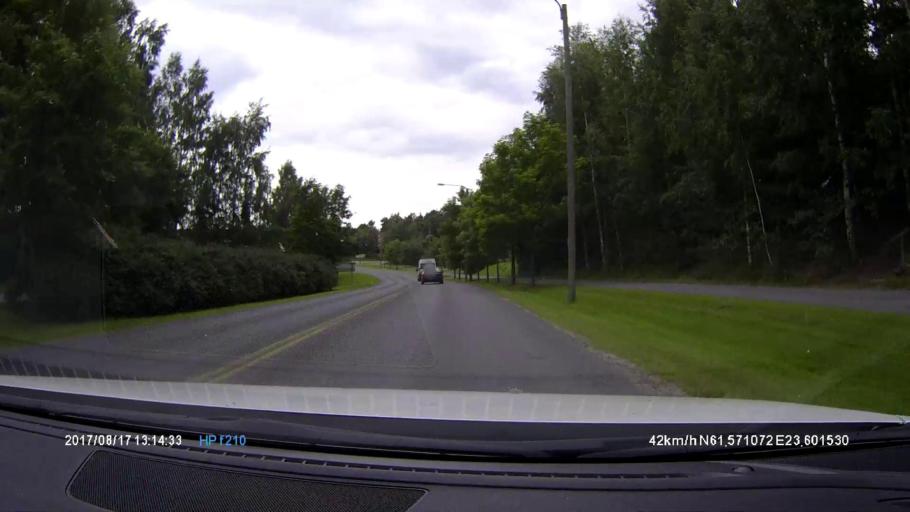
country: FI
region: Pirkanmaa
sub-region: Tampere
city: Yloejaervi
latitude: 61.5710
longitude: 23.6013
